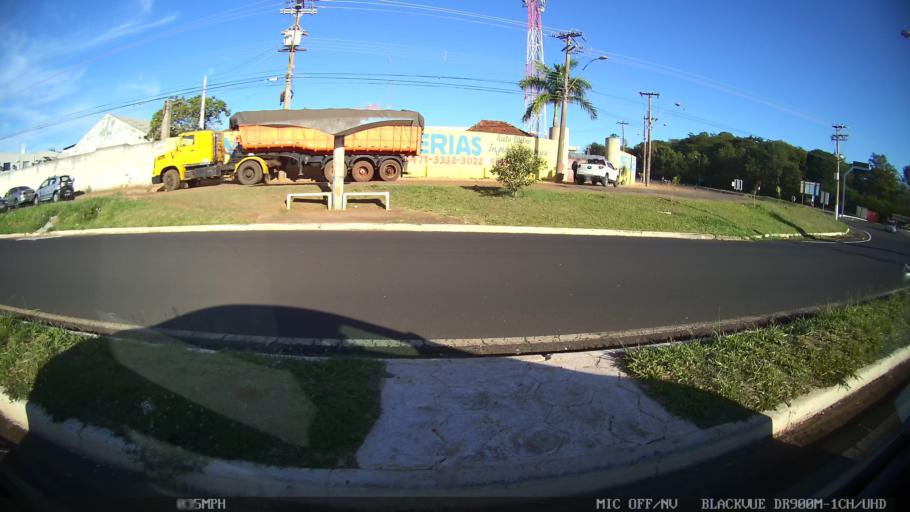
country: BR
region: Sao Paulo
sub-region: Americo Brasiliense
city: Americo Brasiliense
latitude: -21.7448
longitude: -48.1283
